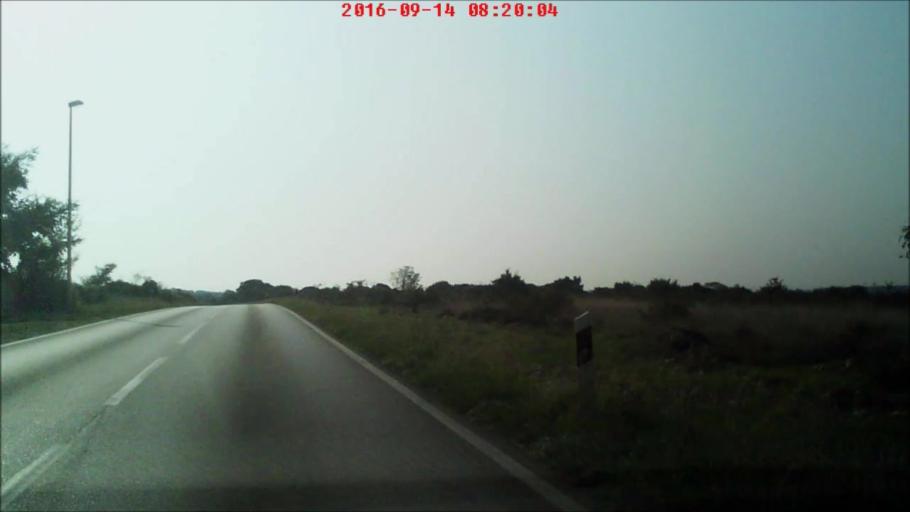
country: HR
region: Zadarska
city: Nin
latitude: 44.2285
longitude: 15.1967
